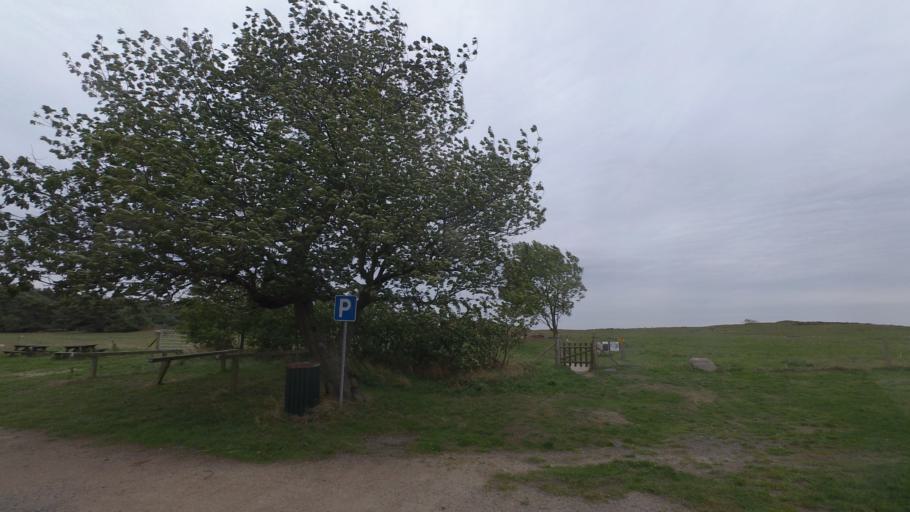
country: DK
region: Capital Region
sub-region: Bornholm Kommune
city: Akirkeby
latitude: 55.0012
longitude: 14.9994
